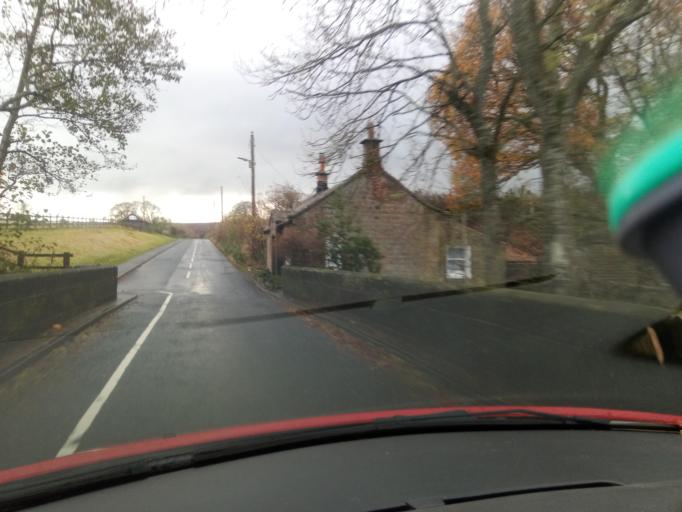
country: GB
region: England
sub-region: Northumberland
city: Birtley
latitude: 55.1431
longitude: -2.2619
